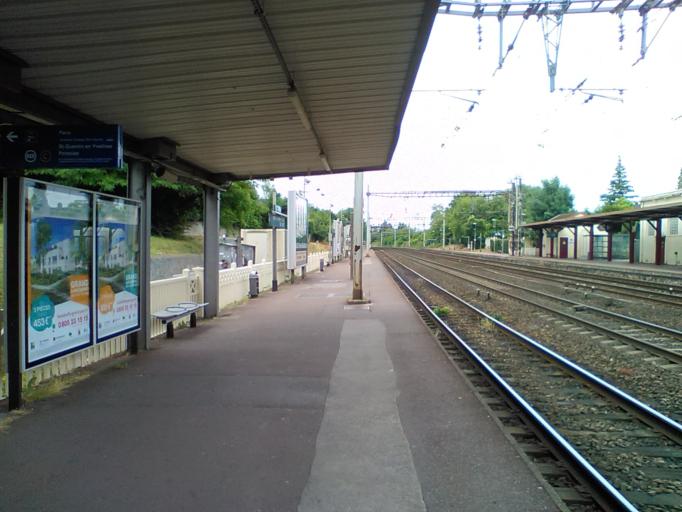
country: FR
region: Ile-de-France
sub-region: Departement de l'Essonne
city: Sainte-Genevieve-des-Bois
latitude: 48.6531
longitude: 2.3134
